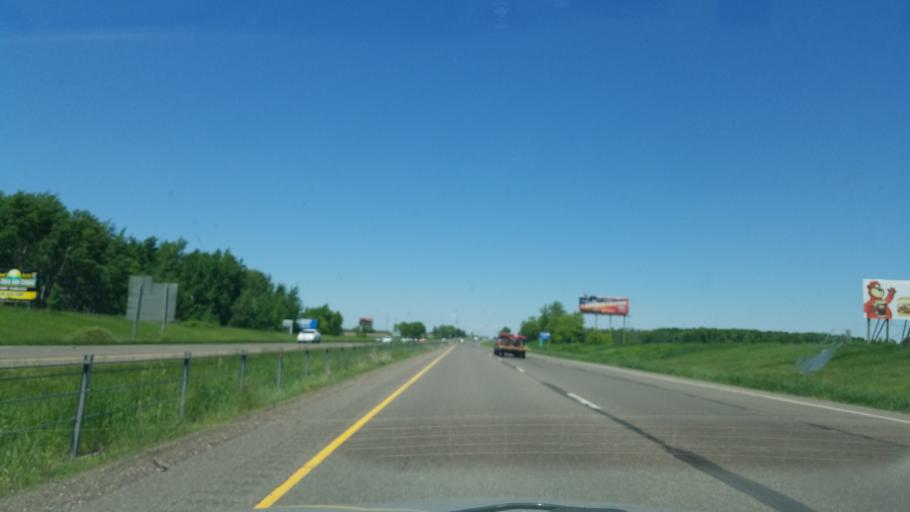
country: US
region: Minnesota
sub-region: Pine County
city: Rock Creek
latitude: 45.7706
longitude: -92.9899
